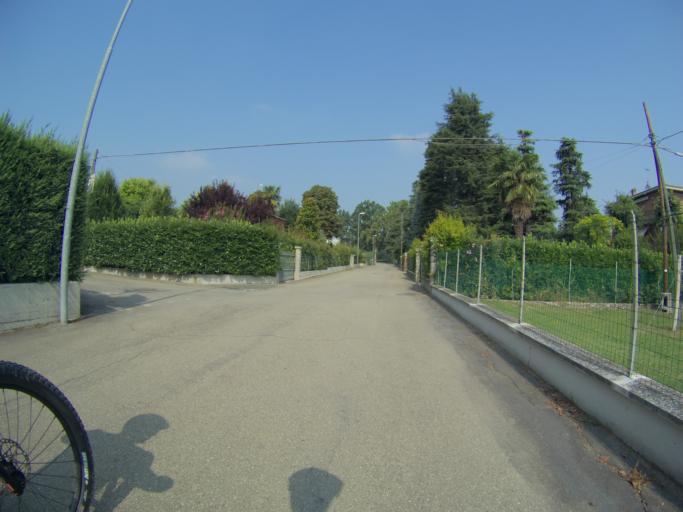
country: IT
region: Emilia-Romagna
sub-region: Provincia di Reggio Emilia
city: Pratissolo
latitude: 44.5958
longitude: 10.6732
